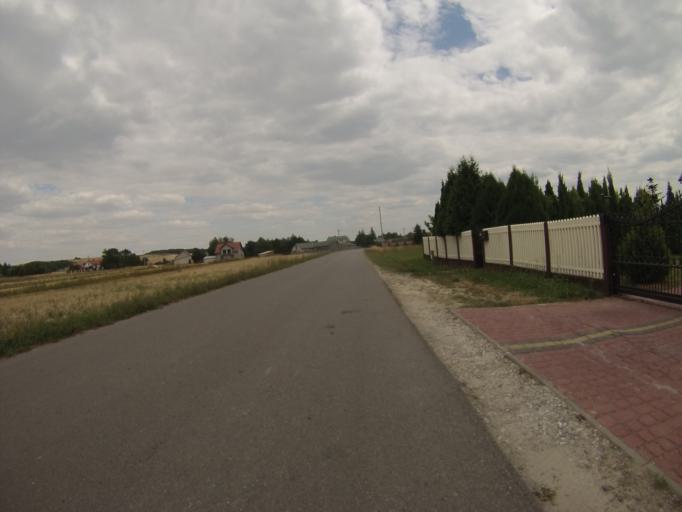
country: PL
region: Swietokrzyskie
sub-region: Powiat staszowski
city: Bogoria
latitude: 50.6867
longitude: 21.2112
